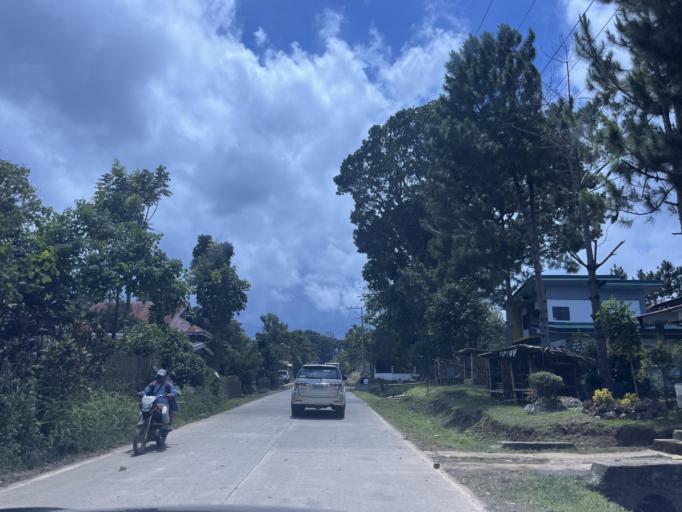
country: PH
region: Northern Mindanao
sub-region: Province of Bukidnon
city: Sumilao
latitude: 8.2876
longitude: 124.9488
